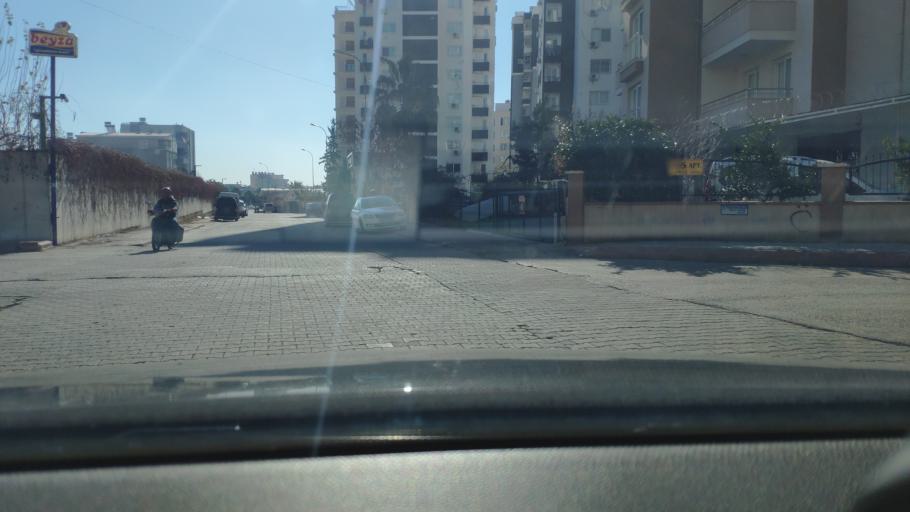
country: TR
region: Adana
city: Seyhan
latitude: 37.0228
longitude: 35.2684
